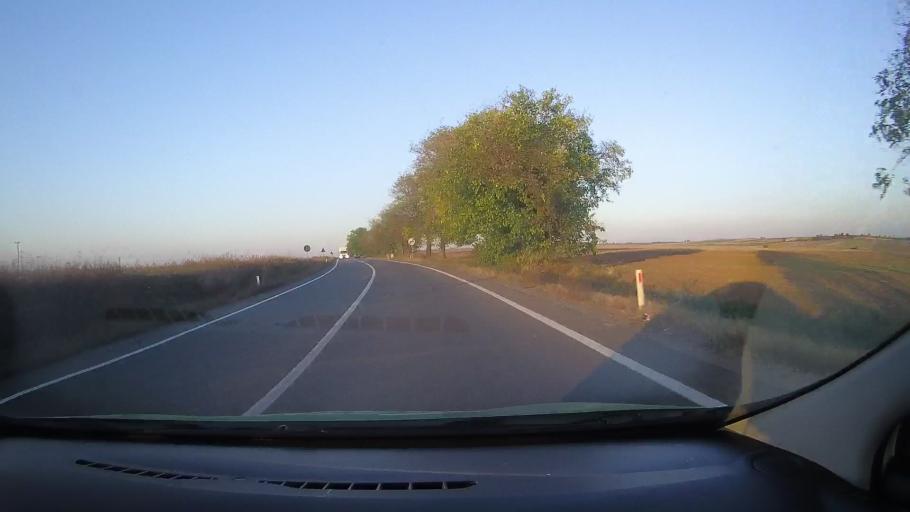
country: RO
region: Bihor
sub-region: Comuna Rosiori
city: Rosiori
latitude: 47.2654
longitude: 21.9712
